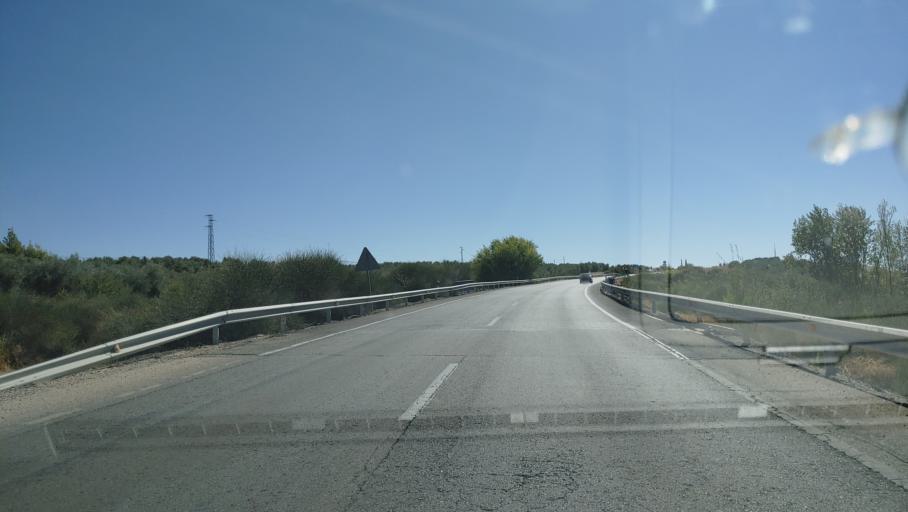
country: ES
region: Andalusia
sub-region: Provincia de Jaen
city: Villacarrillo
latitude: 38.1296
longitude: -3.0578
